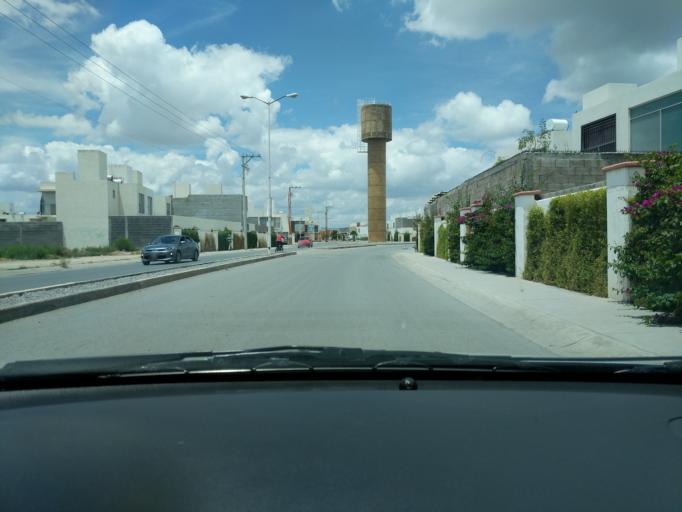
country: MX
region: San Luis Potosi
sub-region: San Luis Potosi
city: Fraccion Milpillas
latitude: 22.2176
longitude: -100.9358
